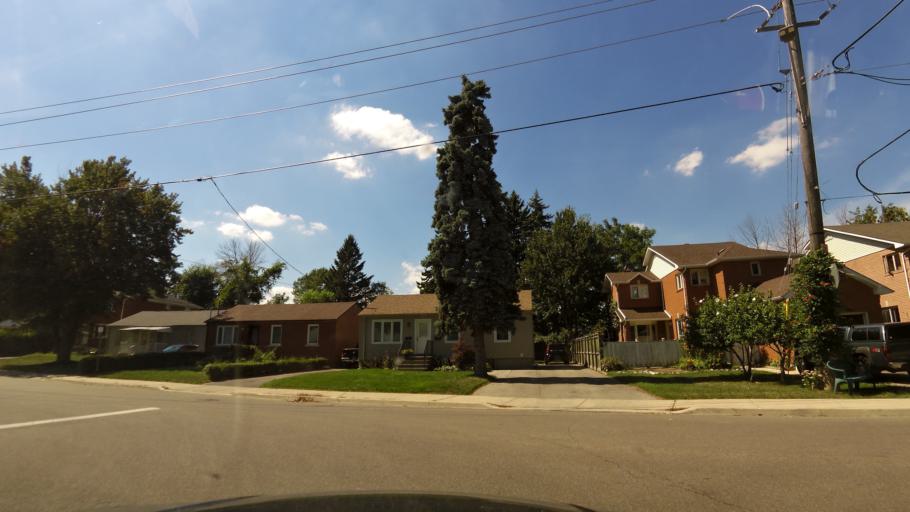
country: CA
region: Ontario
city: Mississauga
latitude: 43.5443
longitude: -79.5991
